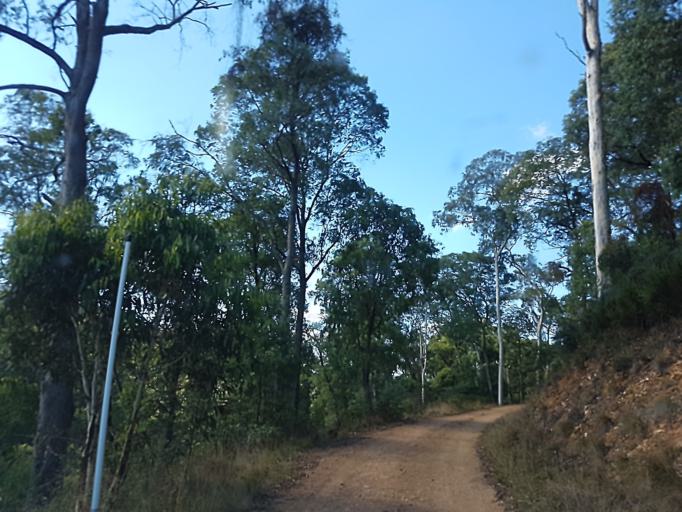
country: AU
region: Victoria
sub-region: Alpine
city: Mount Beauty
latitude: -36.9167
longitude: 147.0439
